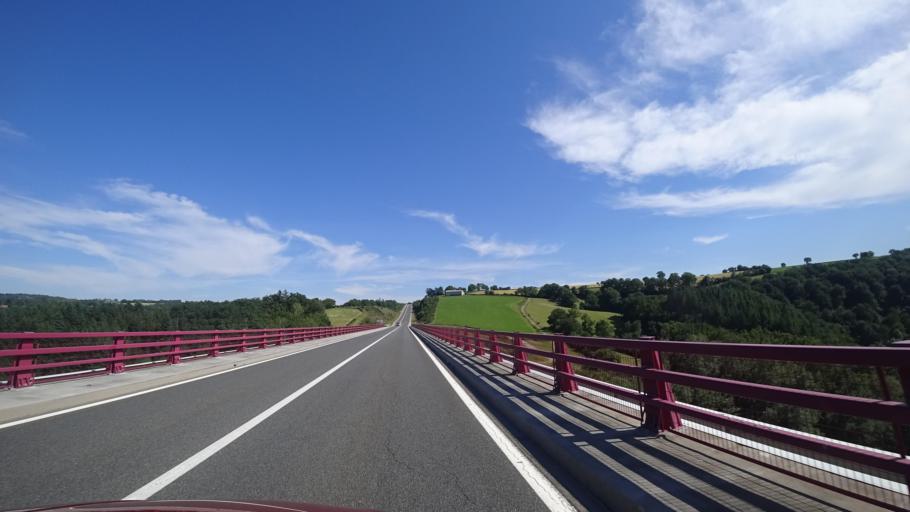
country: FR
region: Midi-Pyrenees
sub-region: Departement de l'Aveyron
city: Pont-de-Salars
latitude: 44.2824
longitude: 2.7193
